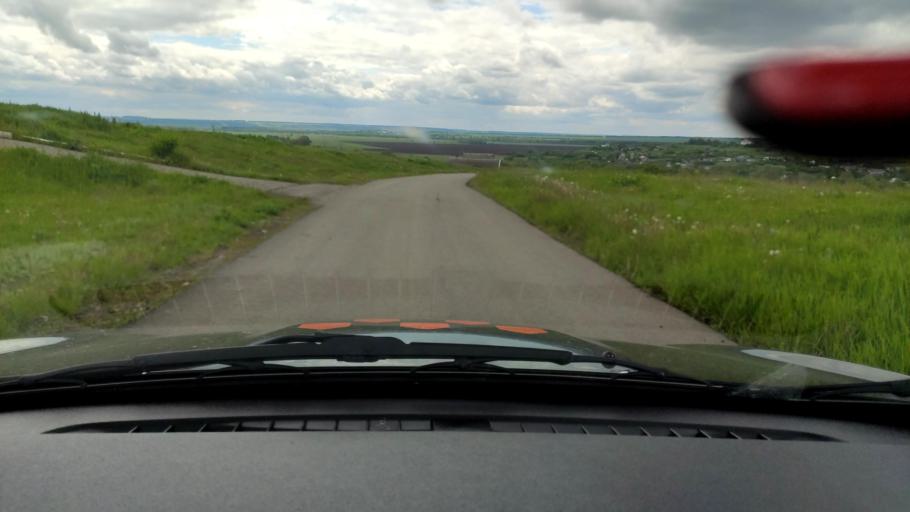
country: RU
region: Voronezj
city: Uryv-Pokrovka
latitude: 51.1085
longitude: 39.1694
